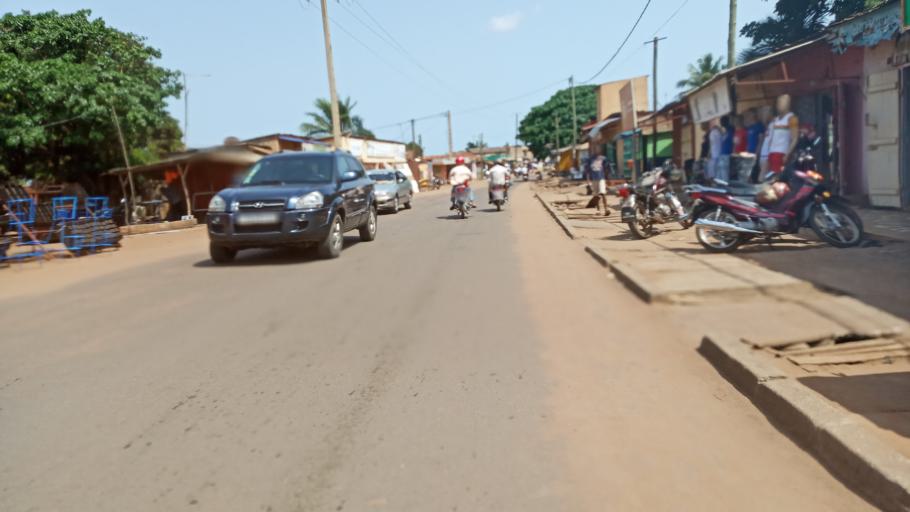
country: TG
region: Maritime
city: Lome
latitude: 6.2237
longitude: 1.2077
